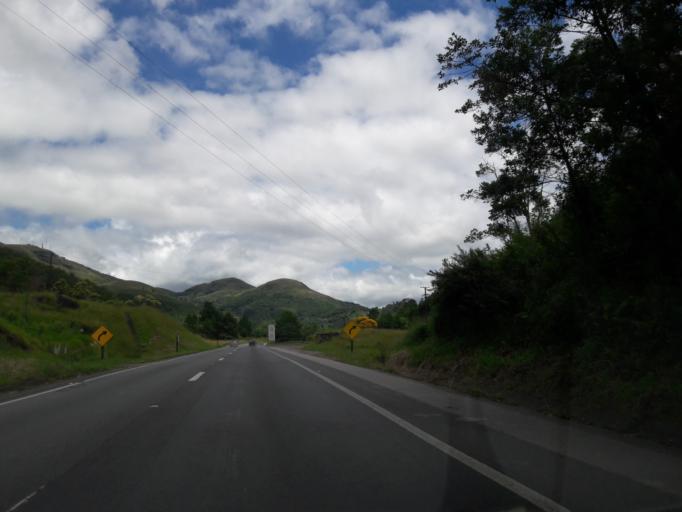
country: BR
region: Parana
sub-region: Campina Grande Do Sul
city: Campina Grande do Sul
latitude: -25.1087
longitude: -48.7966
